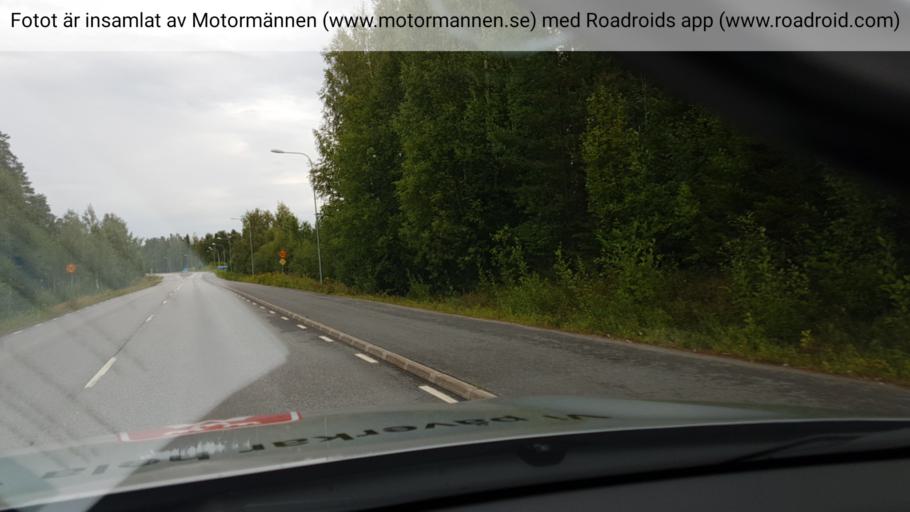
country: SE
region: Norrbotten
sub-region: Bodens Kommun
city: Boden
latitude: 65.8119
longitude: 21.6509
